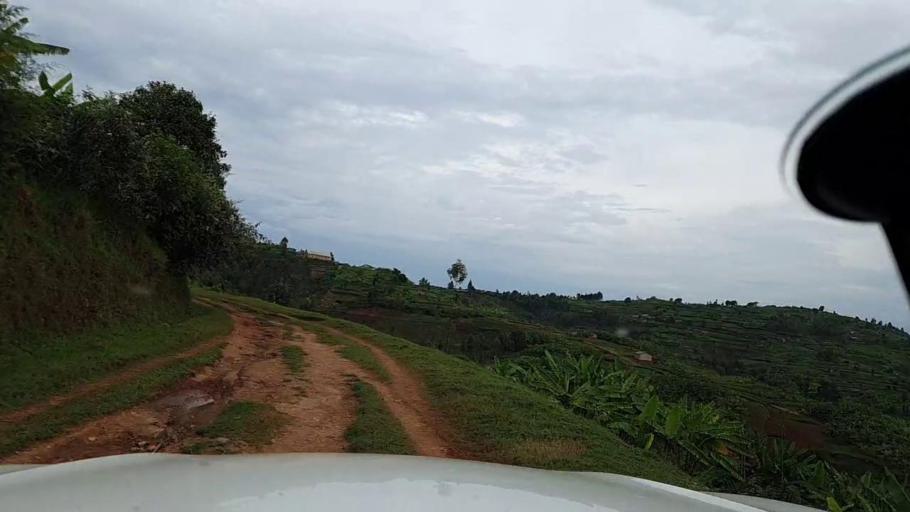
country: RW
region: Southern Province
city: Gitarama
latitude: -2.1240
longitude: 29.6492
